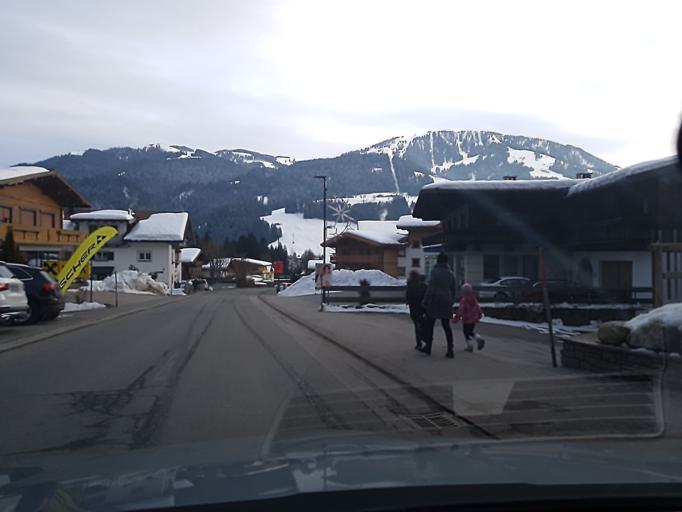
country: AT
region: Tyrol
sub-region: Politischer Bezirk Kufstein
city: Scheffau am Wilden Kaiser
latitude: 47.5280
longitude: 12.2503
